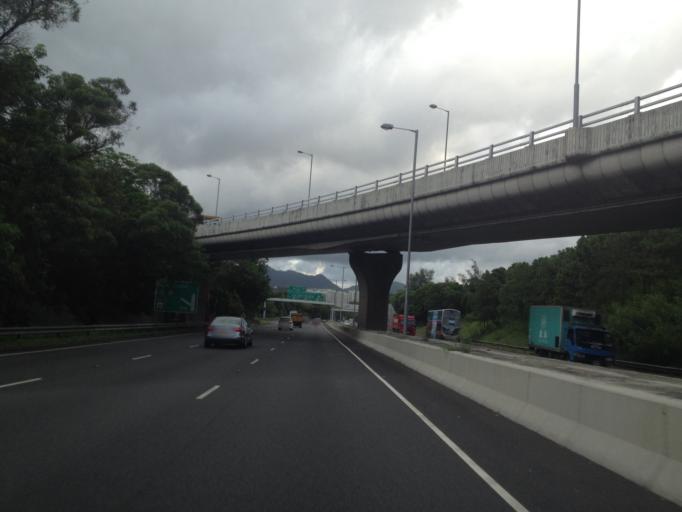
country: HK
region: Sha Tin
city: Sha Tin
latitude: 22.4117
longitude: 114.2124
